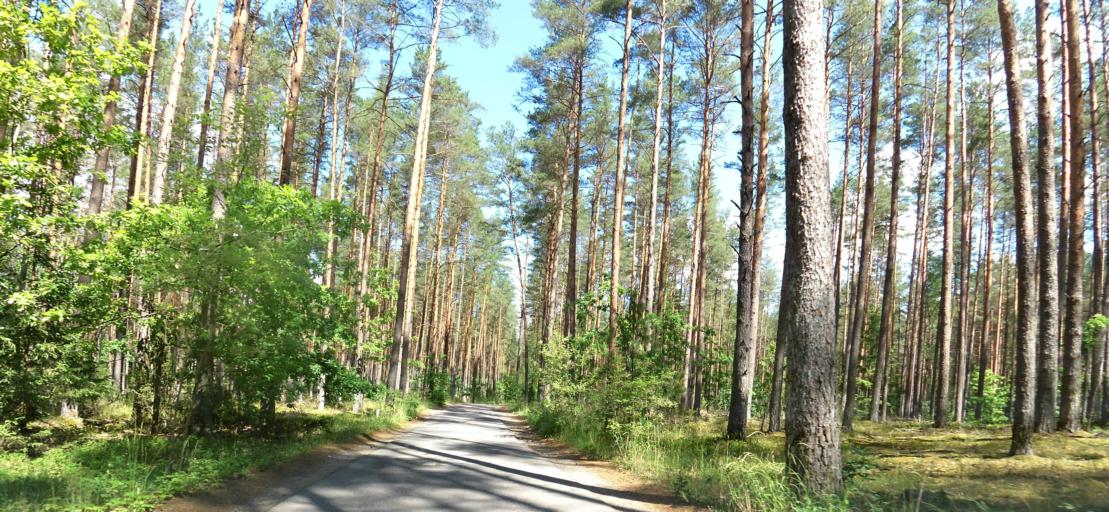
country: LT
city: Nemencine
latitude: 54.8072
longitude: 25.3952
